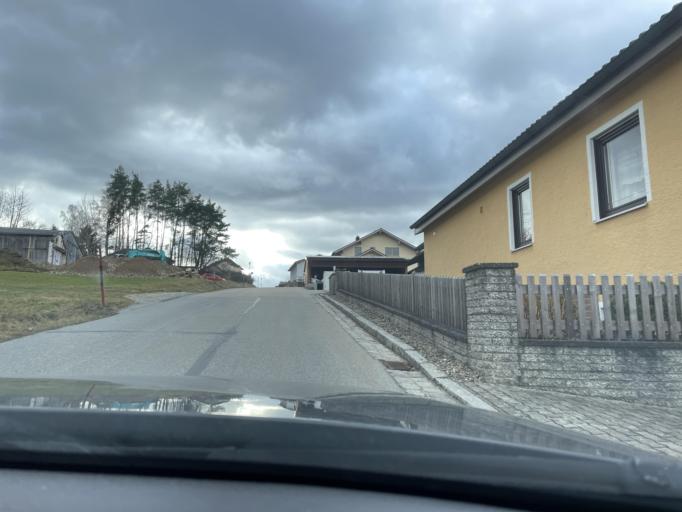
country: DE
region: Bavaria
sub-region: Upper Palatinate
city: Runding
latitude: 49.2206
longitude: 12.7750
